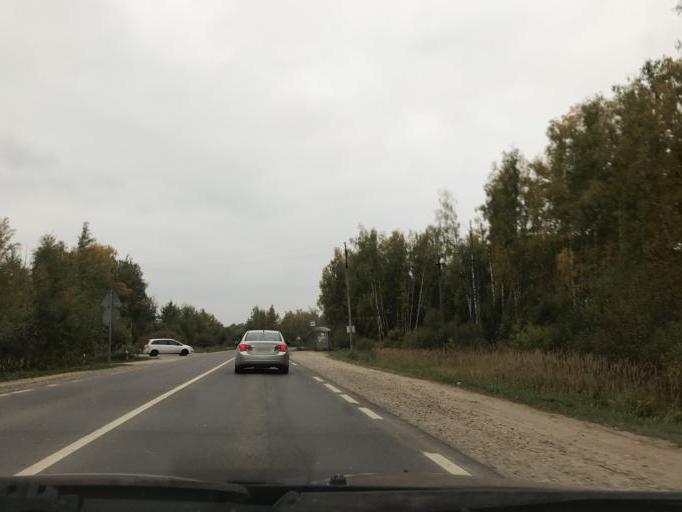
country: RU
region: Kaluga
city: Kaluga
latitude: 54.6190
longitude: 36.2841
